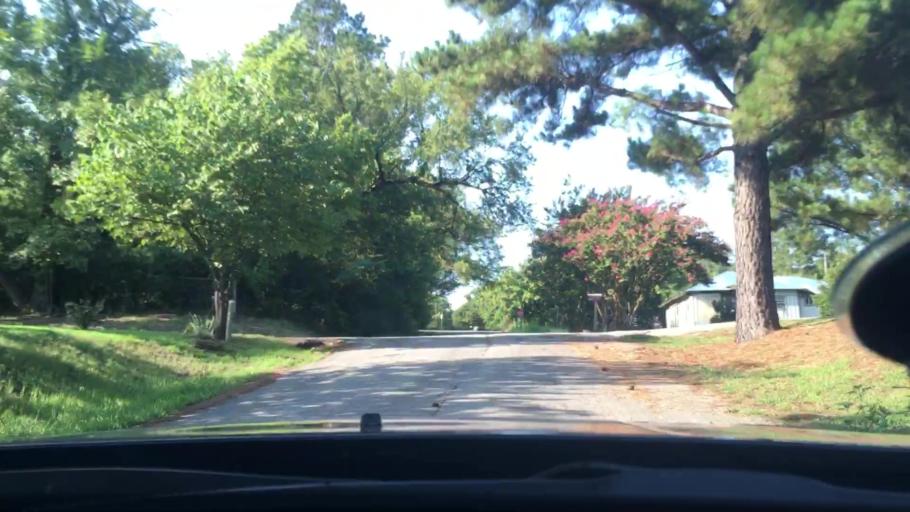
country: US
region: Oklahoma
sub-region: Atoka County
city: Atoka
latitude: 34.3892
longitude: -96.1307
